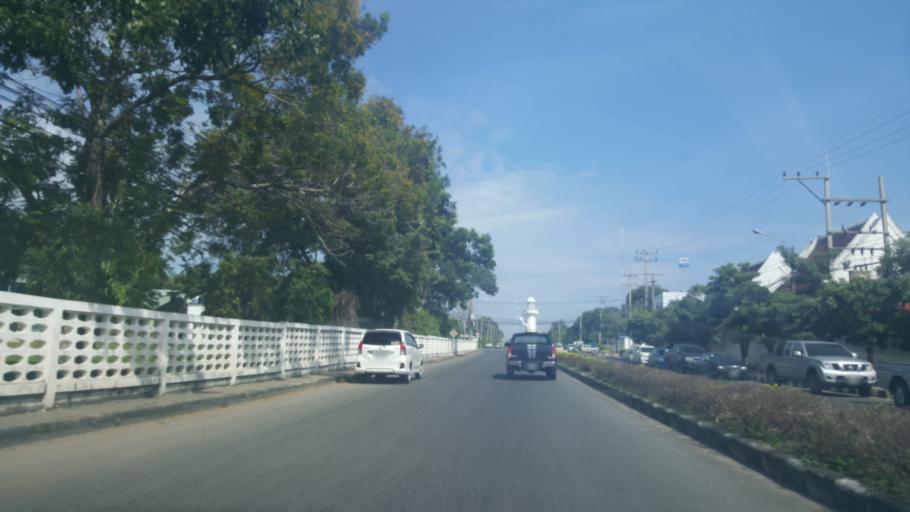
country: TH
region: Chon Buri
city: Sattahip
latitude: 12.6636
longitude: 100.8969
